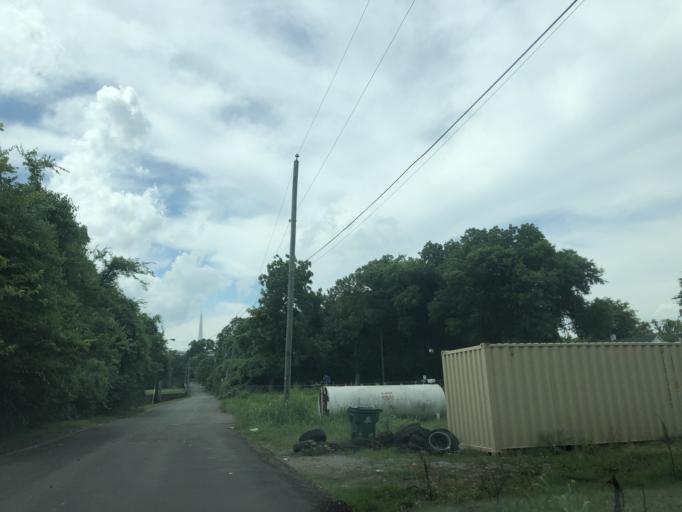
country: US
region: Tennessee
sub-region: Davidson County
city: Nashville
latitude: 36.1978
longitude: -86.7852
